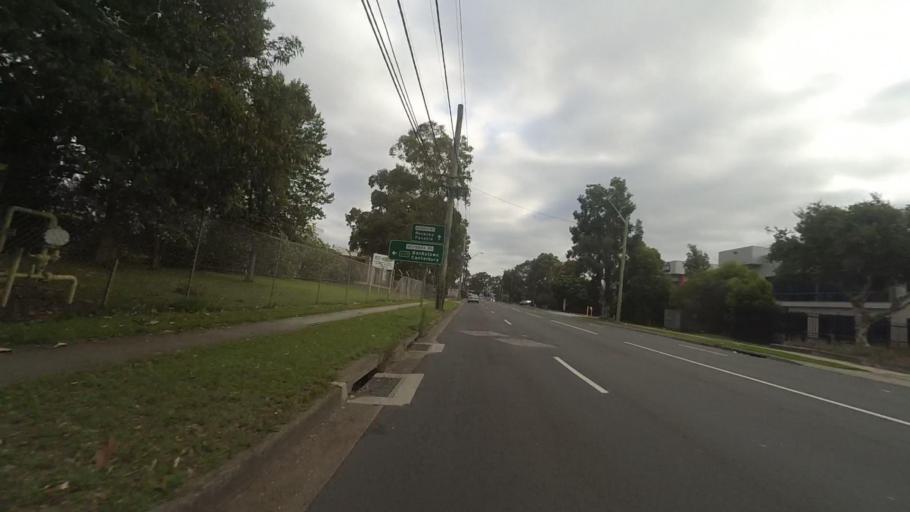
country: AU
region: New South Wales
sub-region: Bankstown
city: Revesby
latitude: -33.9340
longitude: 151.0117
